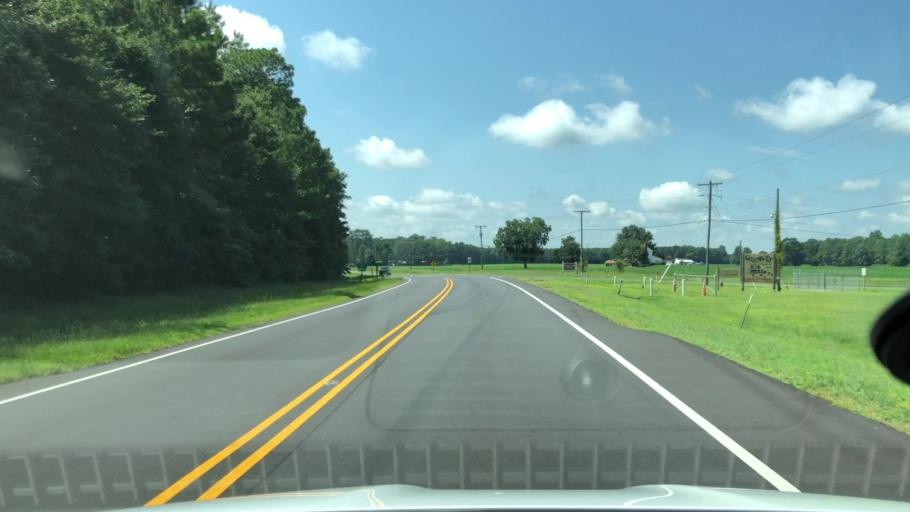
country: US
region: North Carolina
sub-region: Martin County
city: Williamston
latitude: 35.7792
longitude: -77.0641
